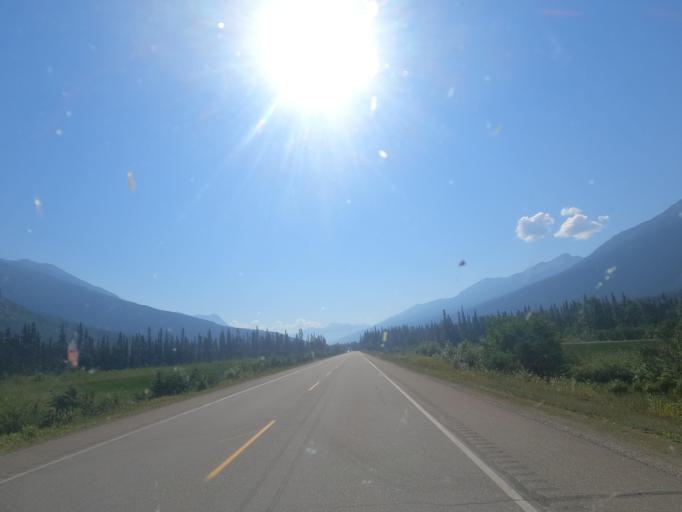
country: CA
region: Alberta
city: Jasper Park Lodge
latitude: 52.9313
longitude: -118.8307
